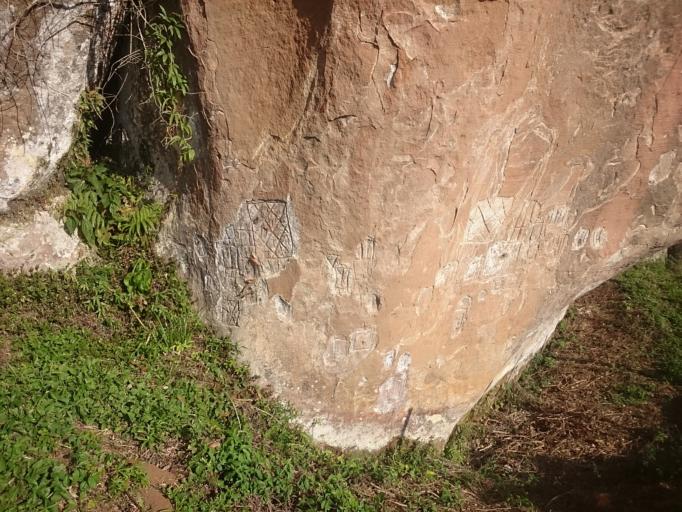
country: BR
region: Santa Catarina
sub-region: Sao Joaquim
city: Sao Joaquim
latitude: -28.0285
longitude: -49.6122
